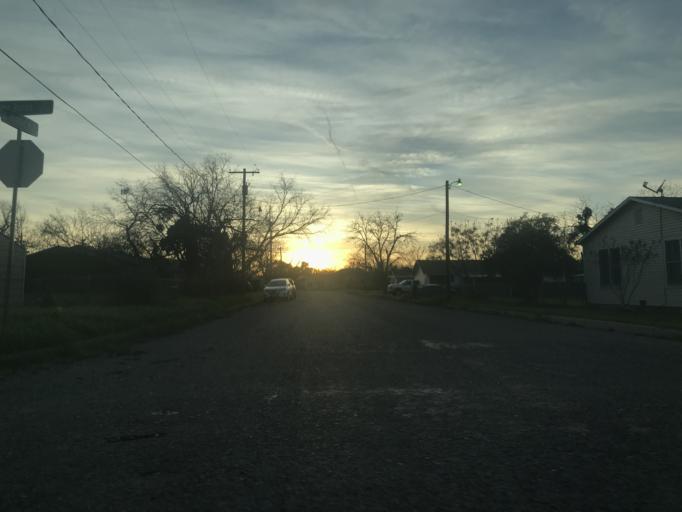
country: US
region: Texas
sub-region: Tom Green County
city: San Angelo
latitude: 31.4439
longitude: -100.4574
